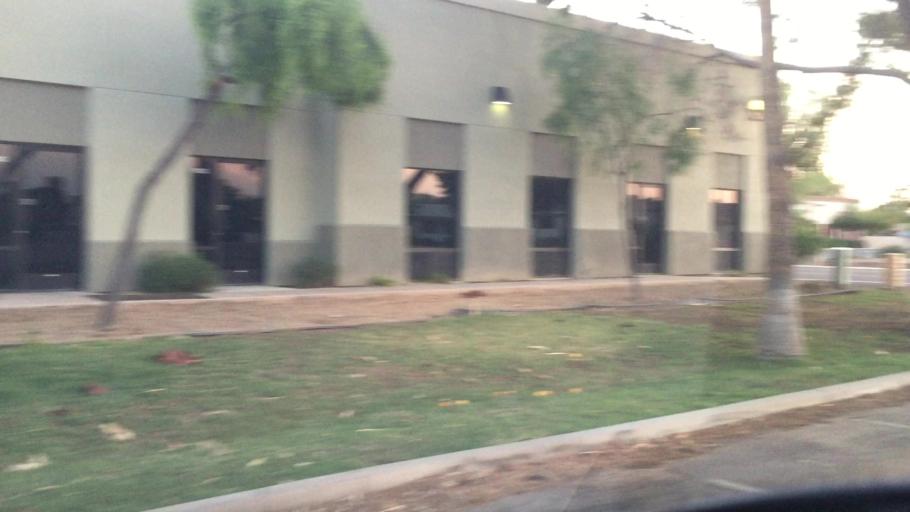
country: US
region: Arizona
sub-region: Maricopa County
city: Tempe
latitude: 33.3945
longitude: -111.9001
